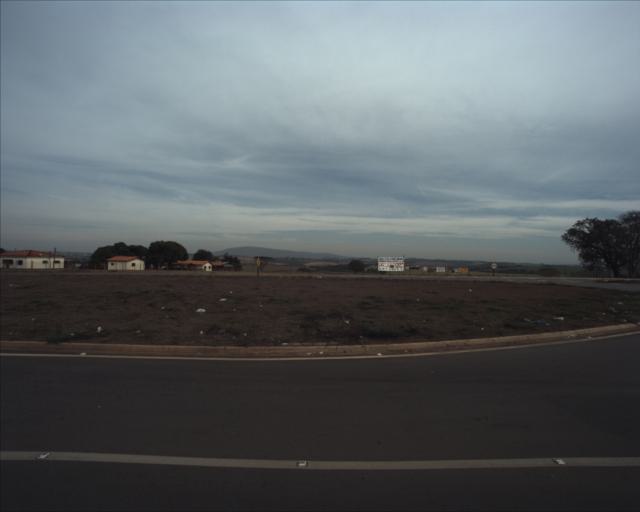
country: BR
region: Sao Paulo
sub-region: Sorocaba
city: Sorocaba
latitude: -23.4179
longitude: -47.5204
